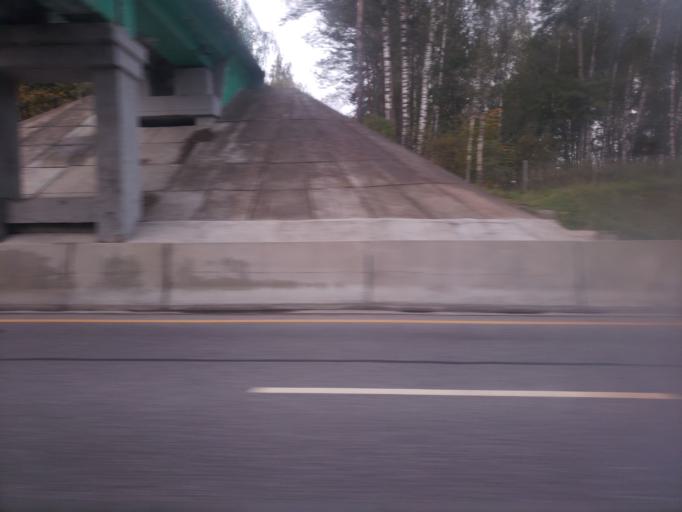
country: RU
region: Moskovskaya
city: Vostryakovo
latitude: 55.4399
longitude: 37.8693
